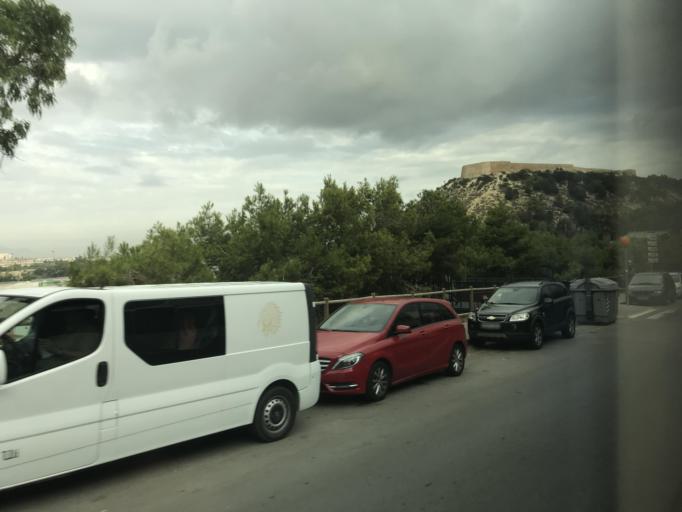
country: ES
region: Valencia
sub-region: Provincia de Alicante
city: Guardamar del Segura
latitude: 38.0881
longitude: -0.6558
